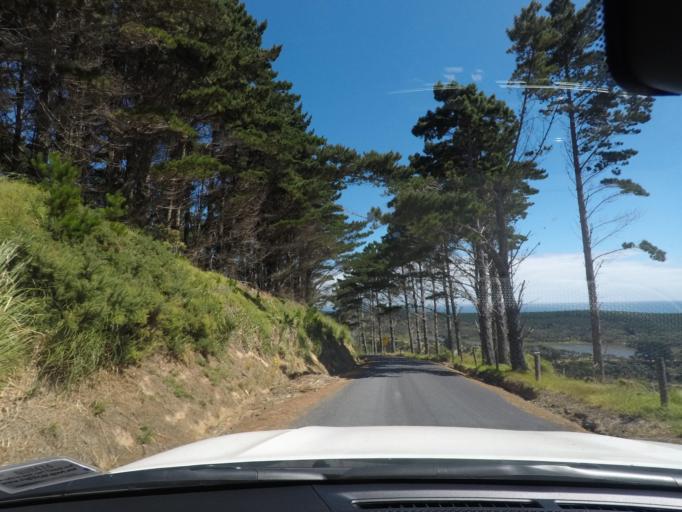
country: NZ
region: Auckland
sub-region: Auckland
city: Parakai
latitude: -36.5875
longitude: 174.2870
